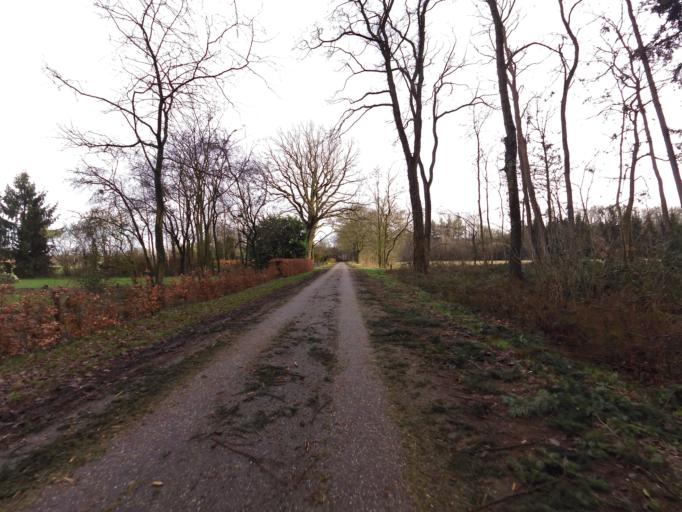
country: NL
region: Gelderland
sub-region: Gemeente Bronckhorst
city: Zelhem
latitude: 51.9718
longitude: 6.3538
